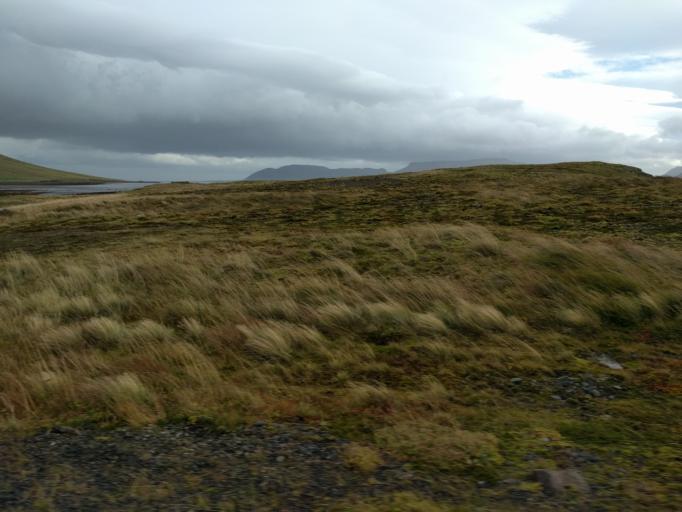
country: IS
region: West
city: Olafsvik
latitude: 64.9252
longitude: -23.3015
